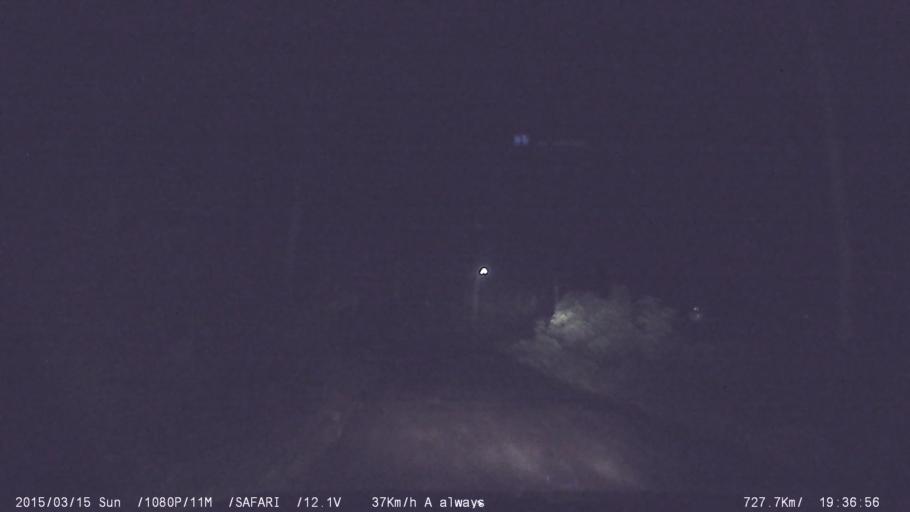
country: IN
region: Kerala
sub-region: Kottayam
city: Palackattumala
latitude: 9.7839
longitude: 76.5643
